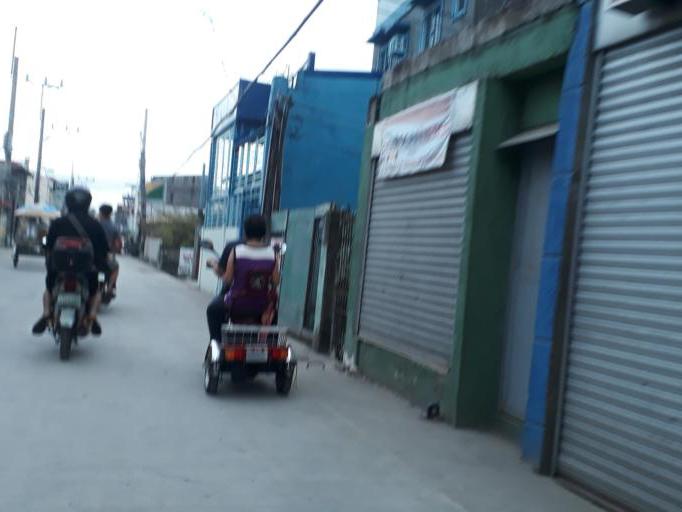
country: PH
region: Central Luzon
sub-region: Province of Bulacan
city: Obando
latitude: 14.7056
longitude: 120.9473
